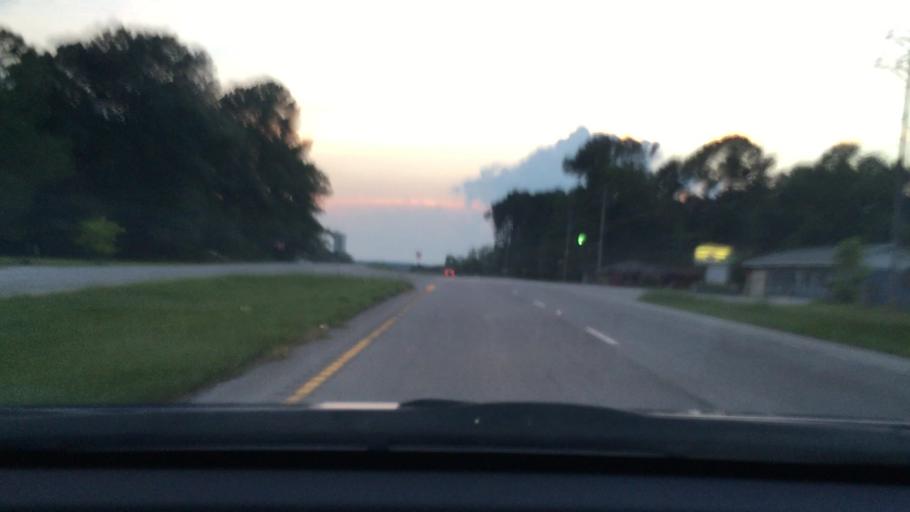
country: US
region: South Carolina
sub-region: Richland County
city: Gadsden
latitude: 33.9437
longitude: -80.7388
